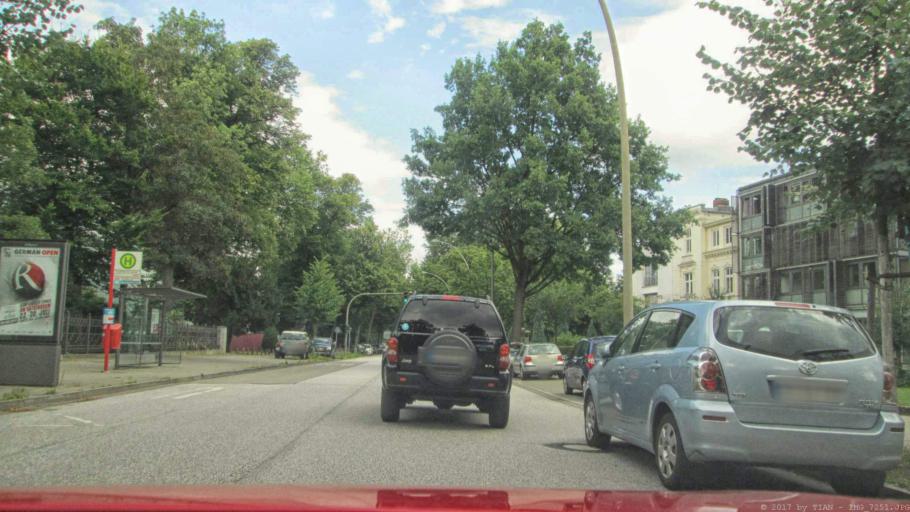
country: DE
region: Hamburg
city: Eimsbuettel
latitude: 53.5764
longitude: 9.9933
